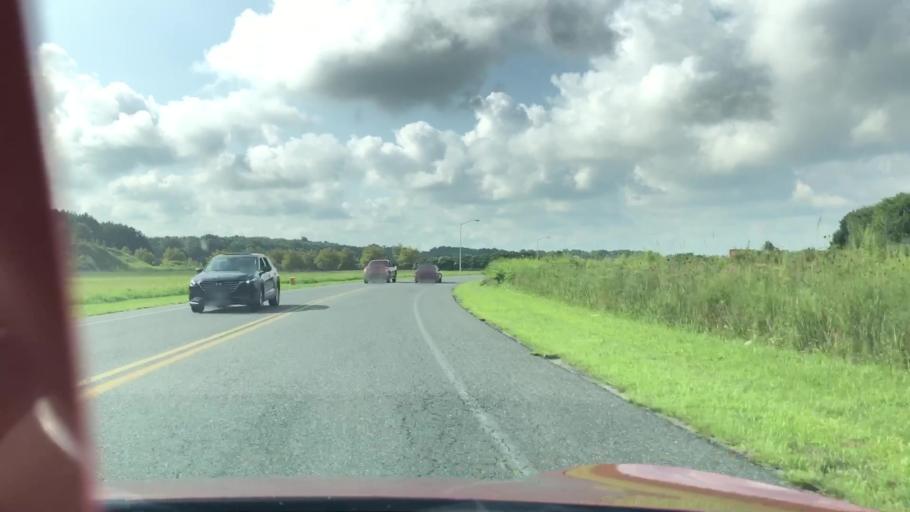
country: US
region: Maryland
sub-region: Wicomico County
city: Delmar
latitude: 38.4060
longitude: -75.5627
